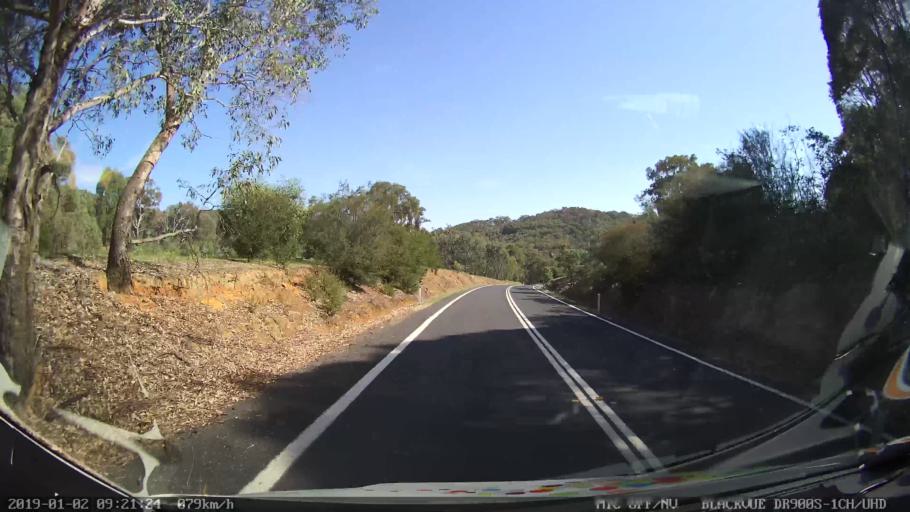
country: AU
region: New South Wales
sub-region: Tumut Shire
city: Tumut
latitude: -35.4062
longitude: 148.2912
